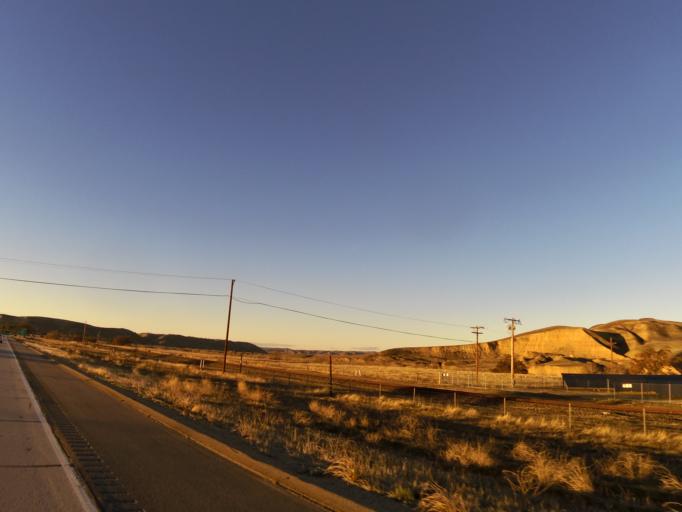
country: US
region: California
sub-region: San Luis Obispo County
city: San Miguel
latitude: 35.7948
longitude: -120.7359
